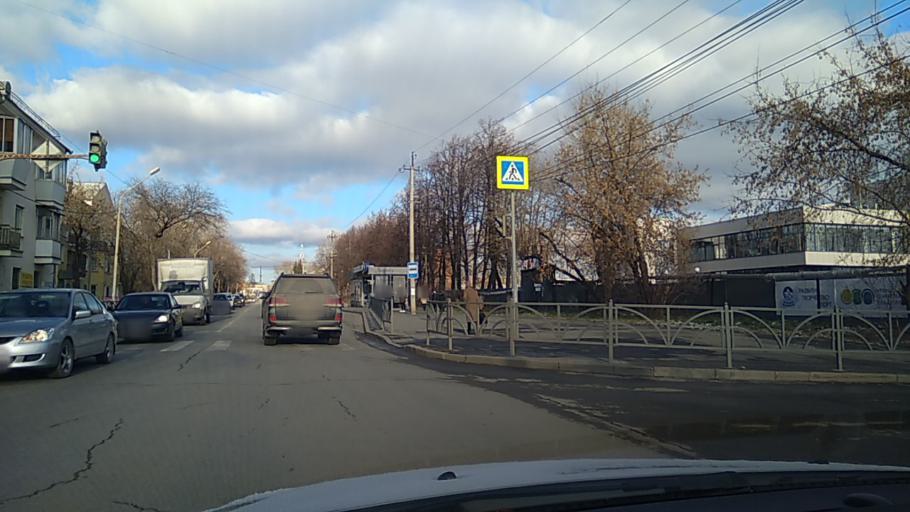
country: RU
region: Sverdlovsk
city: Sovkhoznyy
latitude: 56.7533
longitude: 60.6230
